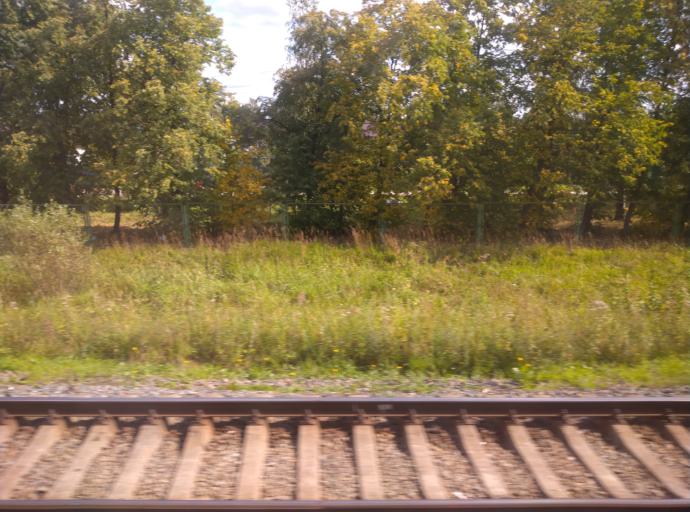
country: RU
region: Leningrad
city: Ul'yanovka
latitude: 59.6311
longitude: 30.7636
